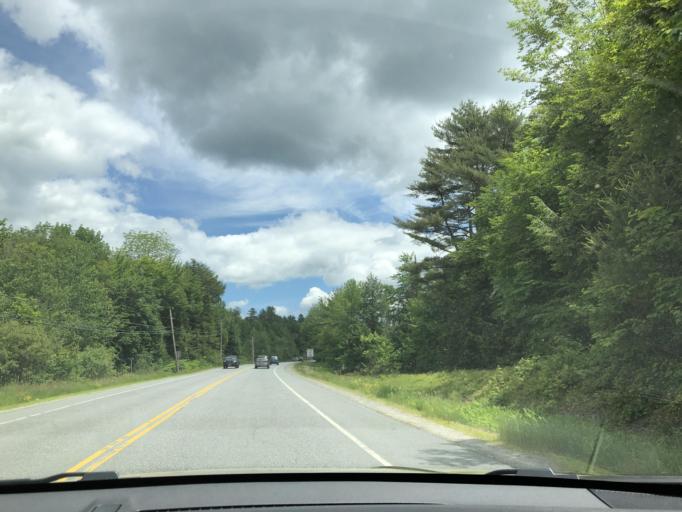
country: US
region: New Hampshire
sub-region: Merrimack County
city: New London
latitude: 43.4266
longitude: -72.0115
